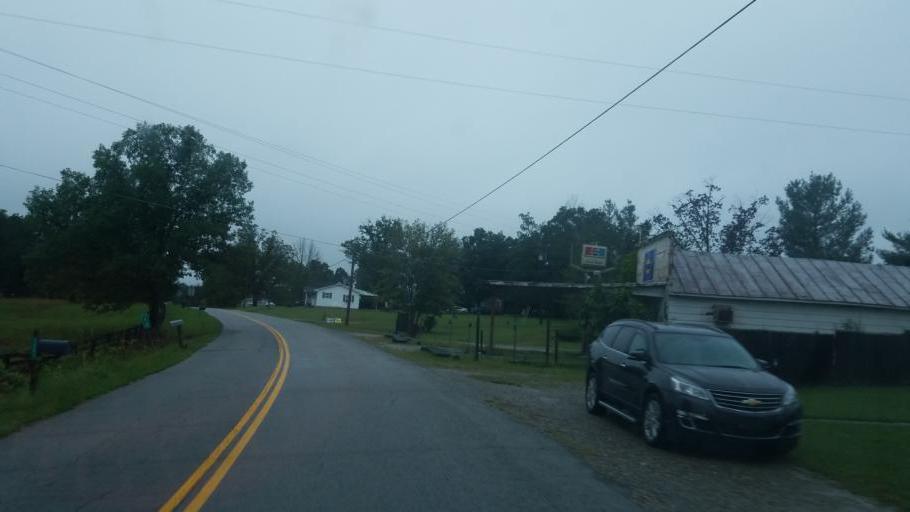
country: US
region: Kentucky
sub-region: Fleming County
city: Flemingsburg
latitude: 38.4051
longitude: -83.6123
